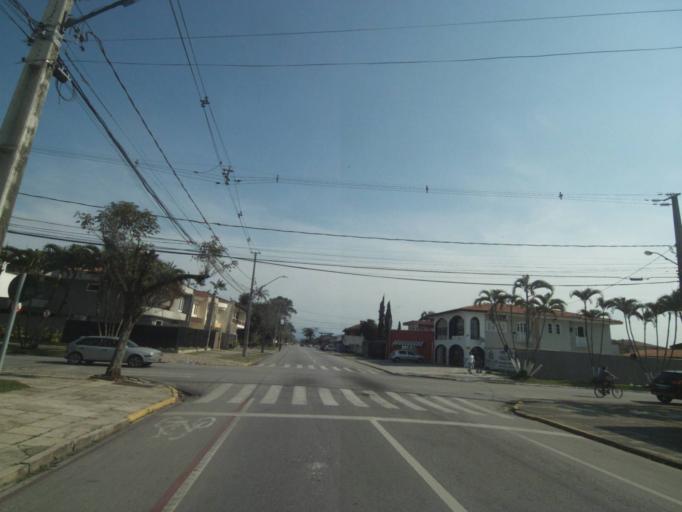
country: BR
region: Parana
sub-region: Paranagua
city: Paranagua
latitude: -25.5237
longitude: -48.5167
